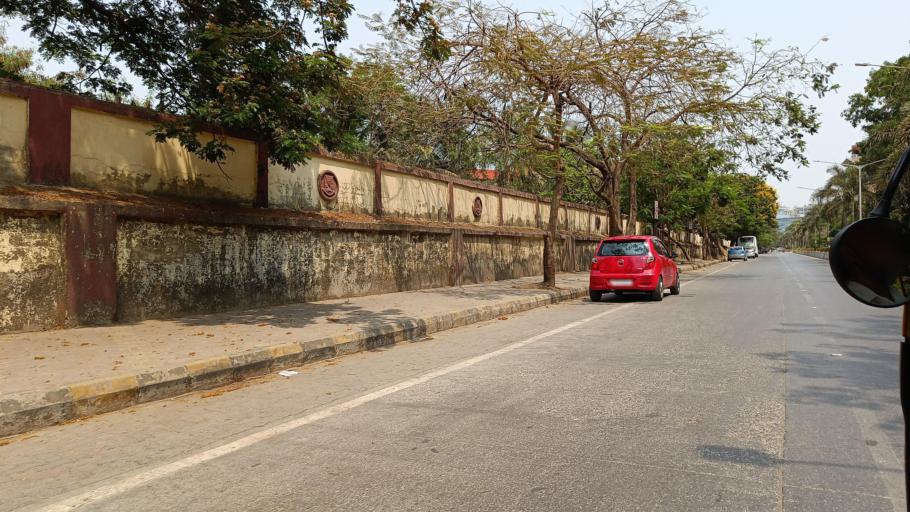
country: IN
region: Maharashtra
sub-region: Mumbai Suburban
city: Mumbai
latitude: 19.0663
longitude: 72.8574
